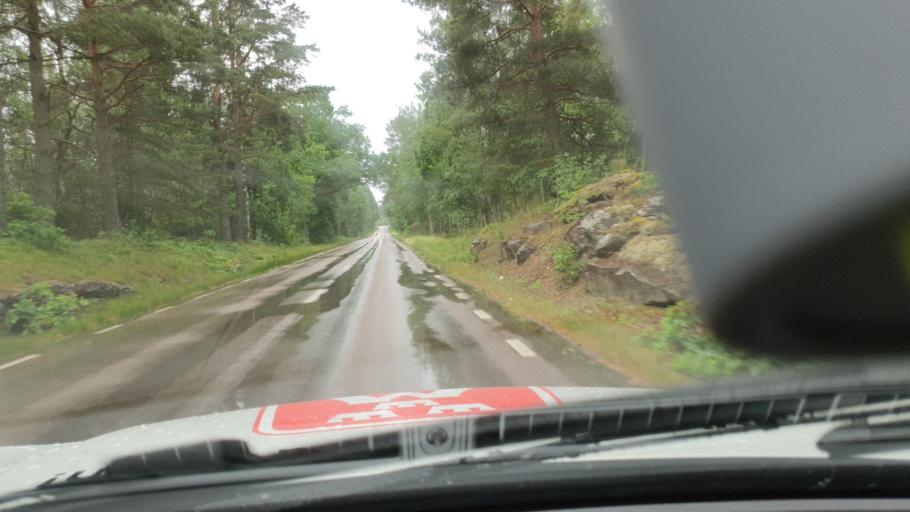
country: SE
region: Vaestra Goetaland
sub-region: Mariestads Kommun
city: Mariestad
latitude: 58.7337
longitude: 13.8944
